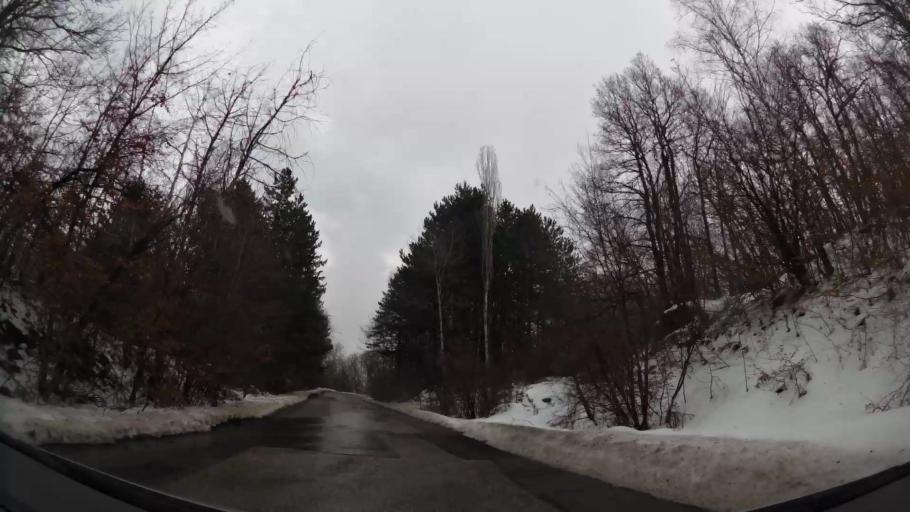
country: BG
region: Sofiya
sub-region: Obshtina Bozhurishte
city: Bozhurishte
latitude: 42.6581
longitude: 23.2044
